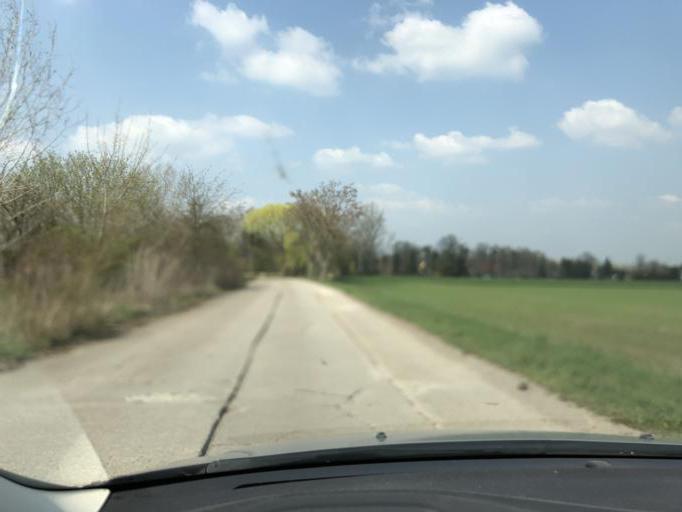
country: DE
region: Saxony-Anhalt
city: Landsberg
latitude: 51.5463
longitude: 12.1377
